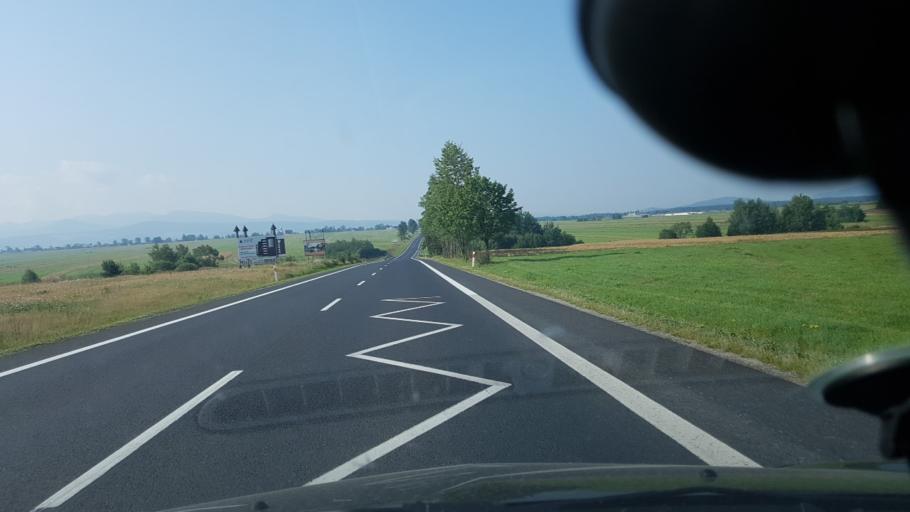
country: PL
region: Lesser Poland Voivodeship
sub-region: Powiat nowotarski
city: Chyzne
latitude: 49.4440
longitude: 19.6836
